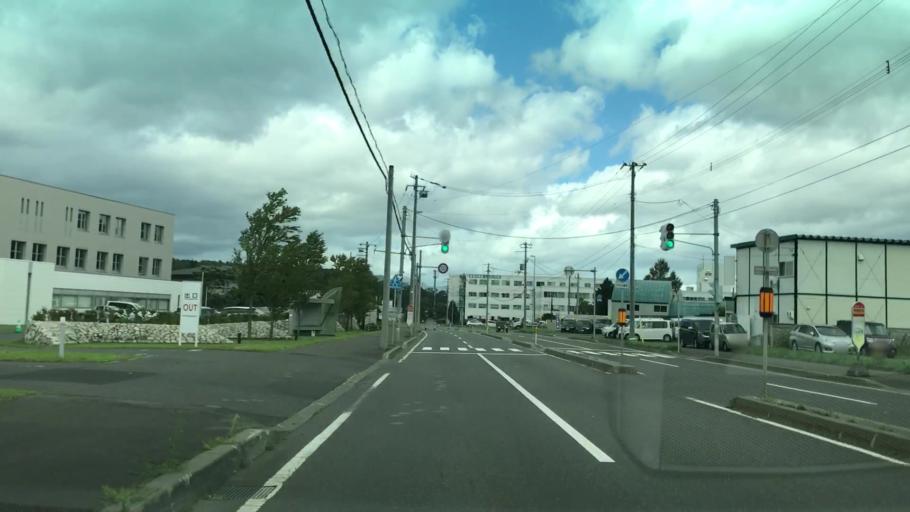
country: JP
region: Hokkaido
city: Kitahiroshima
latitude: 42.9771
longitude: 141.4460
